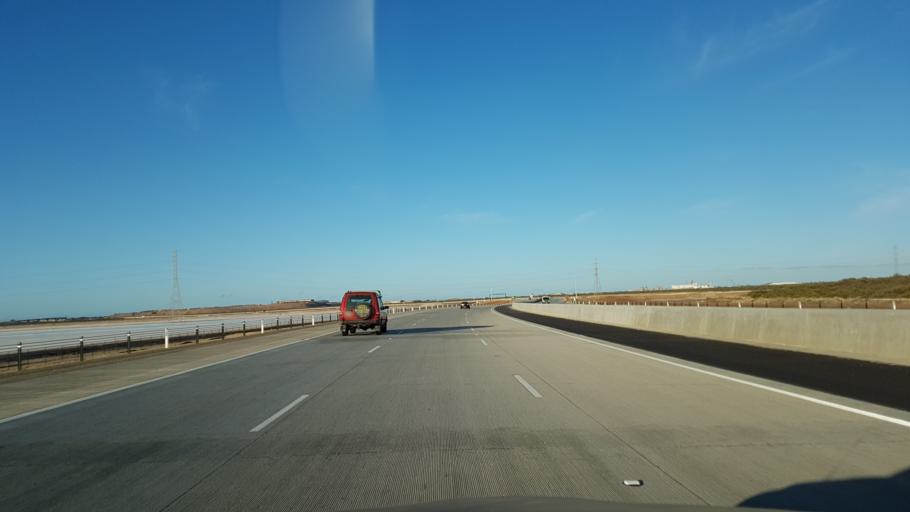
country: AU
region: South Australia
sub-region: Port Adelaide Enfield
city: Enfield
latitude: -34.8064
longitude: 138.5723
